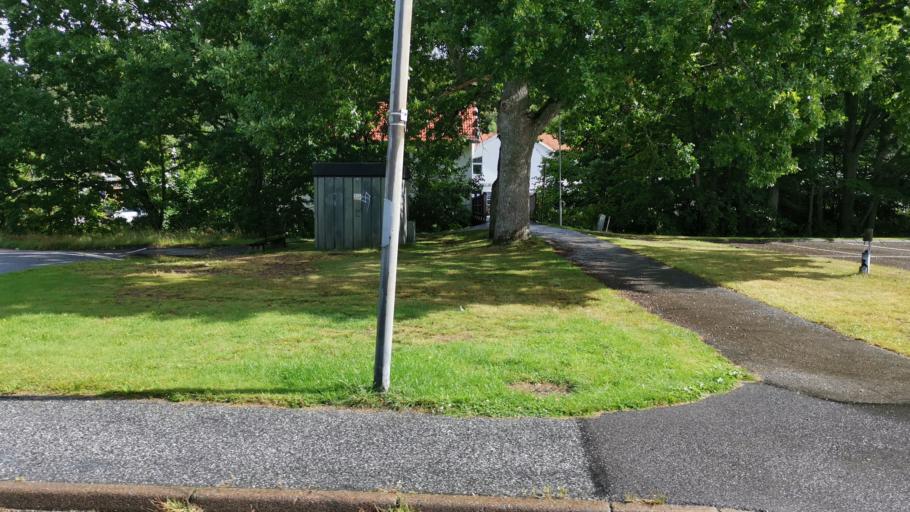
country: SE
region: Vaestra Goetaland
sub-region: Orust
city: Henan
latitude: 58.2344
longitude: 11.6793
